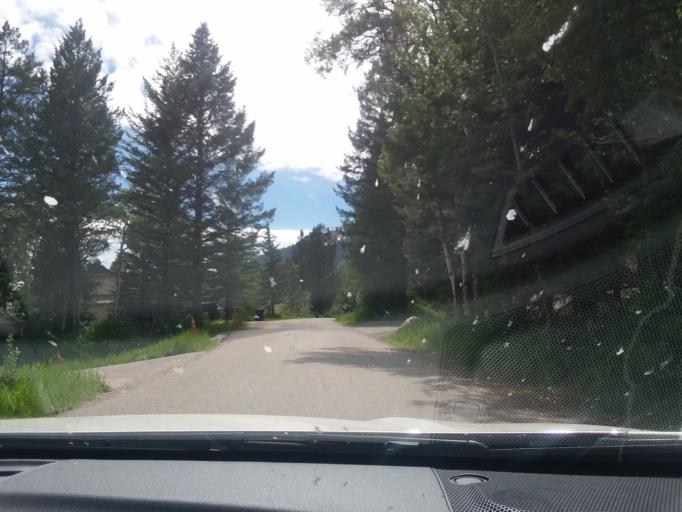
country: US
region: Wyoming
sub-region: Teton County
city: Moose Wilson Road
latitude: 43.5872
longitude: -110.8332
